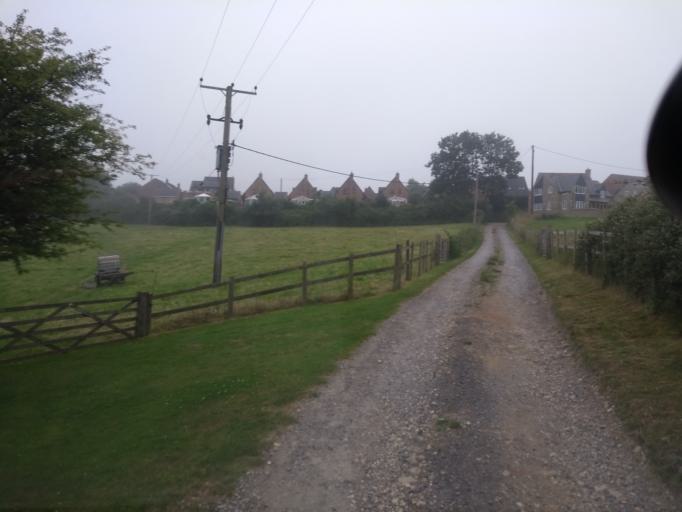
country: GB
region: England
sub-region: Dorset
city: Bridport
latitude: 50.7694
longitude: -2.7713
